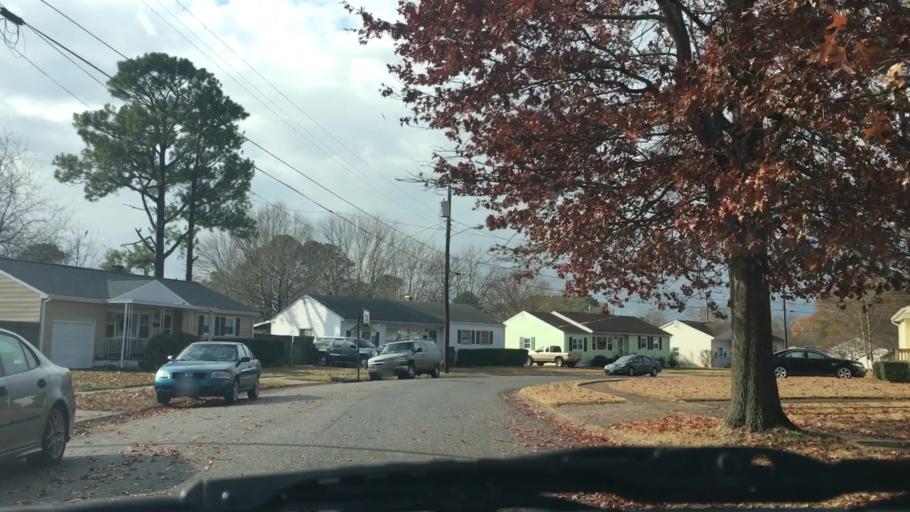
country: US
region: Virginia
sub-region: City of Norfolk
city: Norfolk
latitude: 36.9292
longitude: -76.2302
